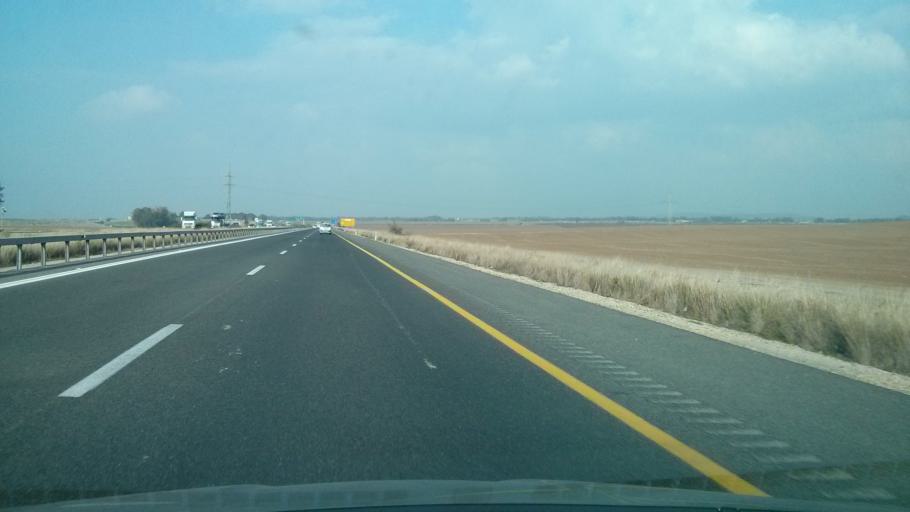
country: IL
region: Central District
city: Gedera
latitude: 31.7687
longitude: 34.8300
